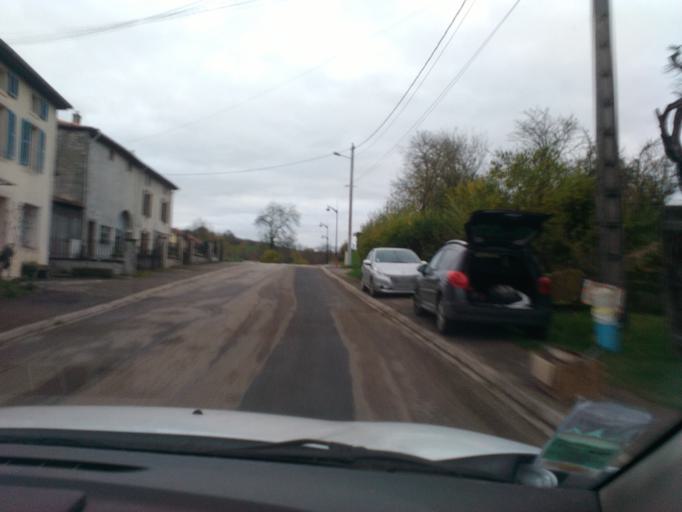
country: FR
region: Lorraine
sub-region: Departement des Vosges
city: Darnieulles
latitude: 48.2528
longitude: 6.2826
